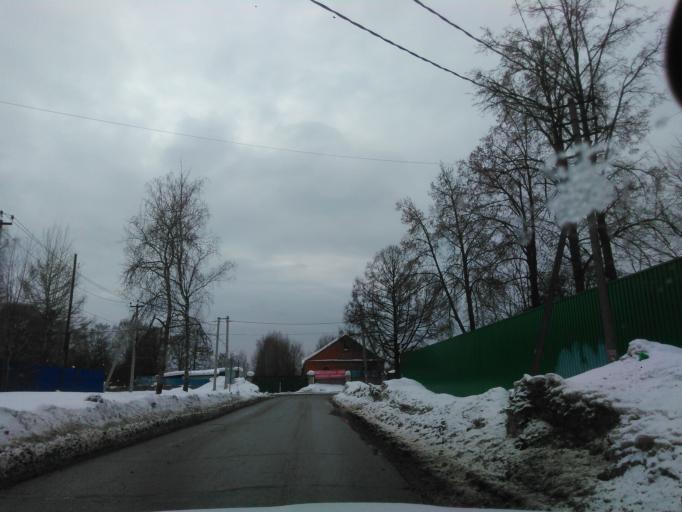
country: RU
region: Moskovskaya
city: Andreyevka
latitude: 55.9764
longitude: 37.1341
